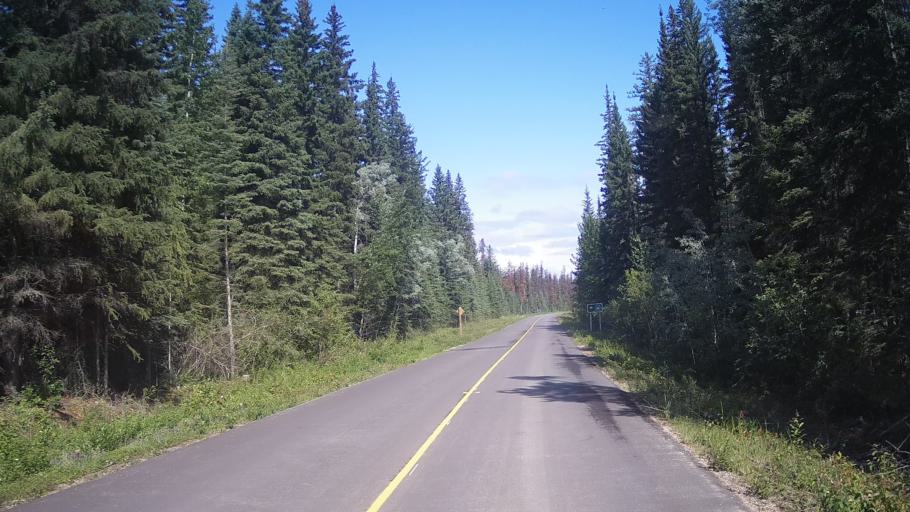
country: CA
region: Alberta
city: Jasper Park Lodge
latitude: 52.7455
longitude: -117.9715
